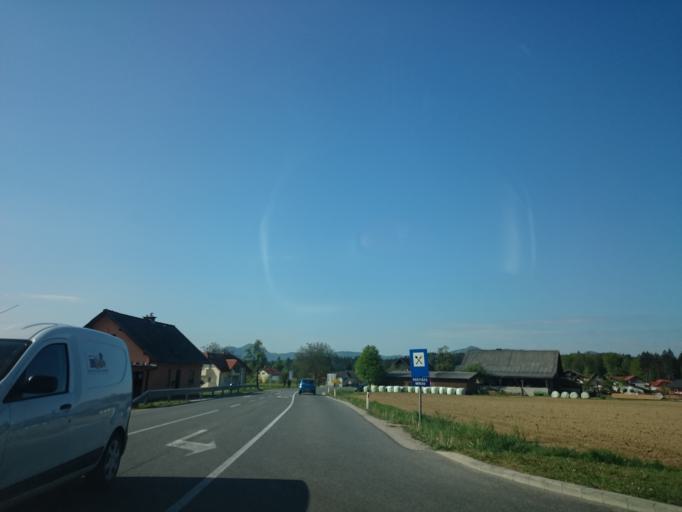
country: SI
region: Sentjur pri Celju
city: Sentjur
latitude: 46.2600
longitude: 15.3918
